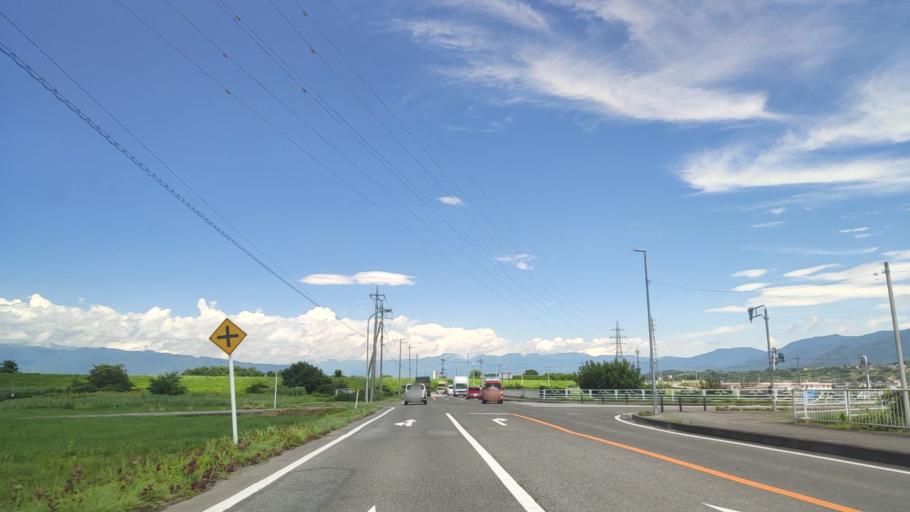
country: JP
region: Yamanashi
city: Ryuo
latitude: 35.5716
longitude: 138.5085
